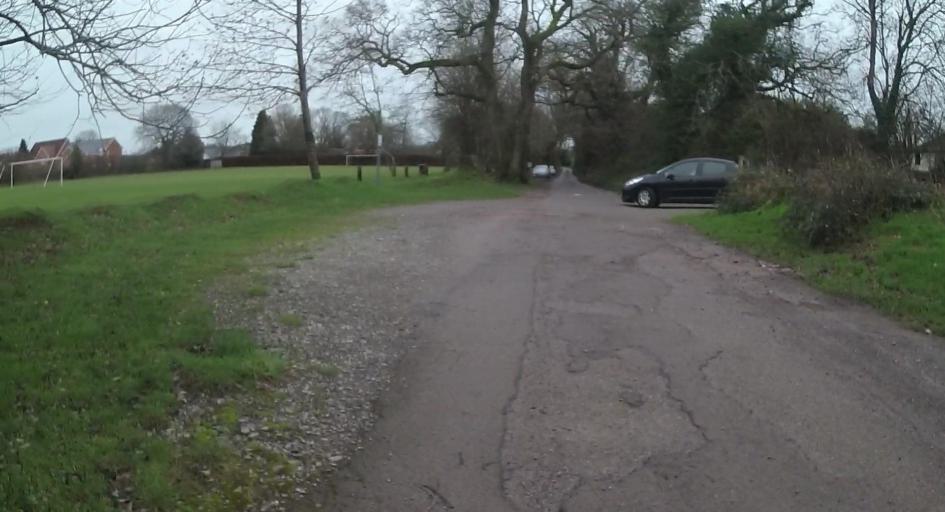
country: GB
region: England
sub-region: Hampshire
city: Four Marks
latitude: 51.1046
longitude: -1.0552
